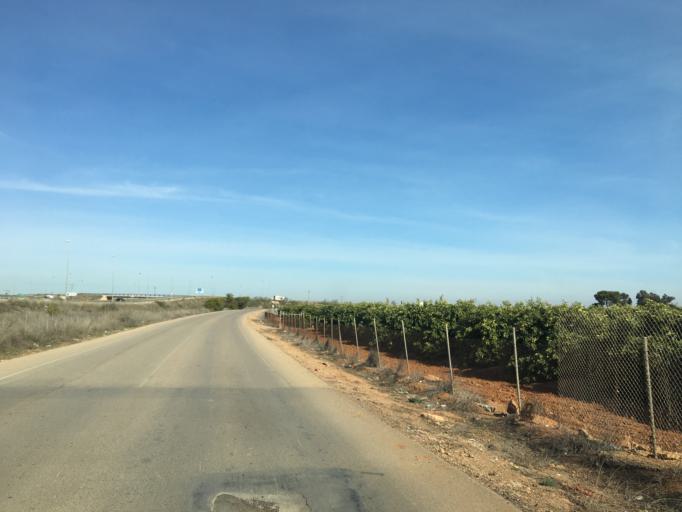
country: ES
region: Murcia
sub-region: Murcia
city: Cartagena
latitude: 37.6600
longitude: -1.0243
